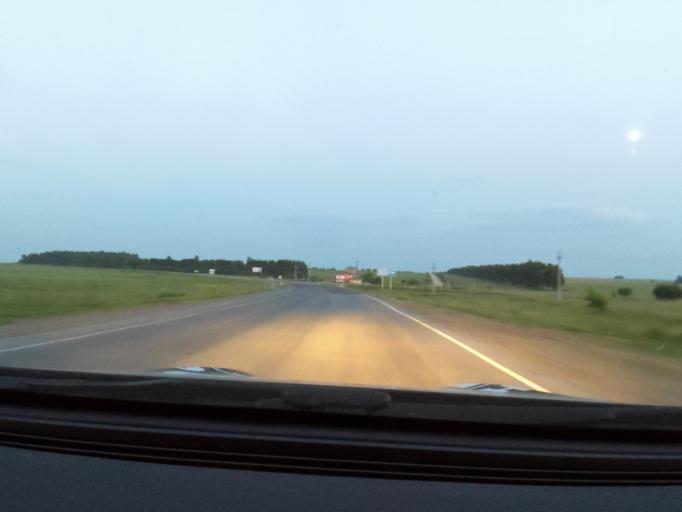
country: RU
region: Bashkortostan
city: Duvan
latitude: 56.0795
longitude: 58.0869
